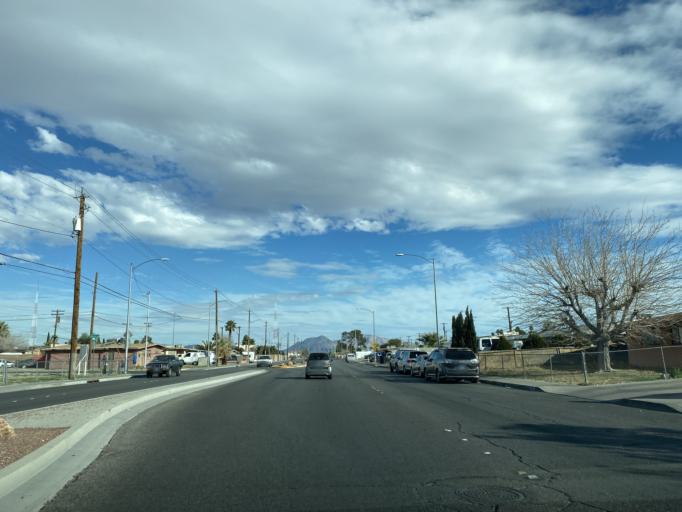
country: US
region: Nevada
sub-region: Clark County
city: Las Vegas
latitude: 36.1885
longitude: -115.1841
